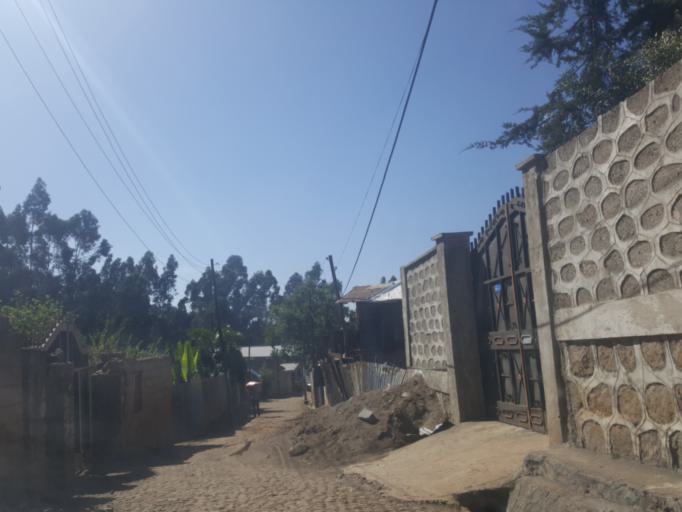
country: ET
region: Adis Abeba
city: Addis Ababa
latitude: 9.0680
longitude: 38.7283
